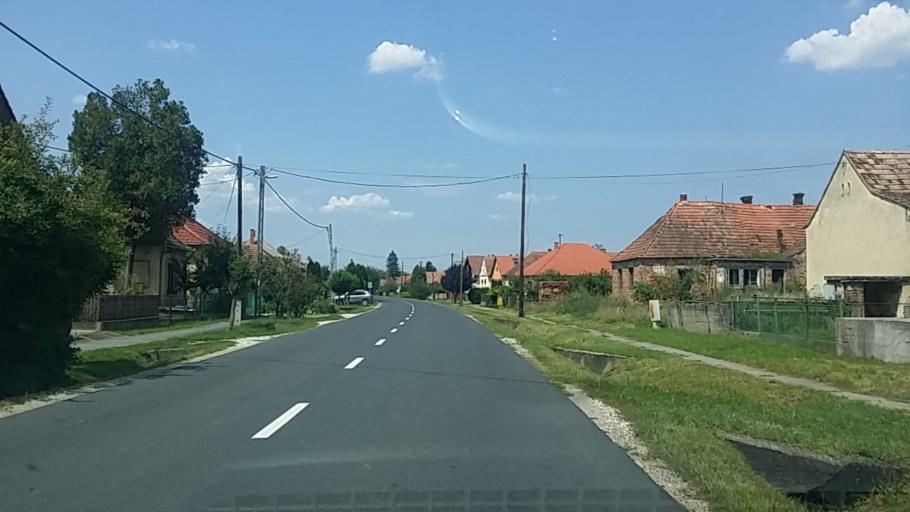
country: HR
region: Medimurska
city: Podturen
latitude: 46.5238
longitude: 16.5554
